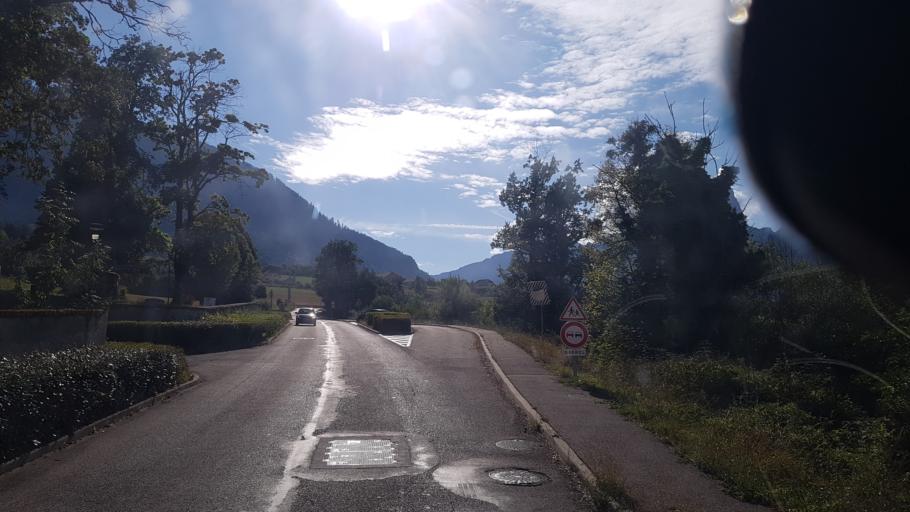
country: FR
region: Rhone-Alpes
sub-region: Departement de l'Isere
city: Mens
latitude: 44.8285
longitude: 5.6173
